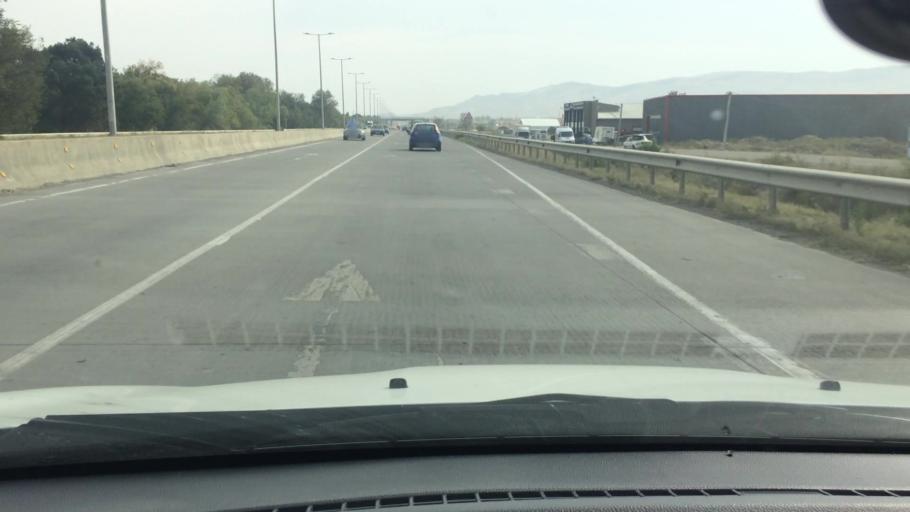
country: GE
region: Kvemo Kartli
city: Rust'avi
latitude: 41.6187
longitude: 44.9285
